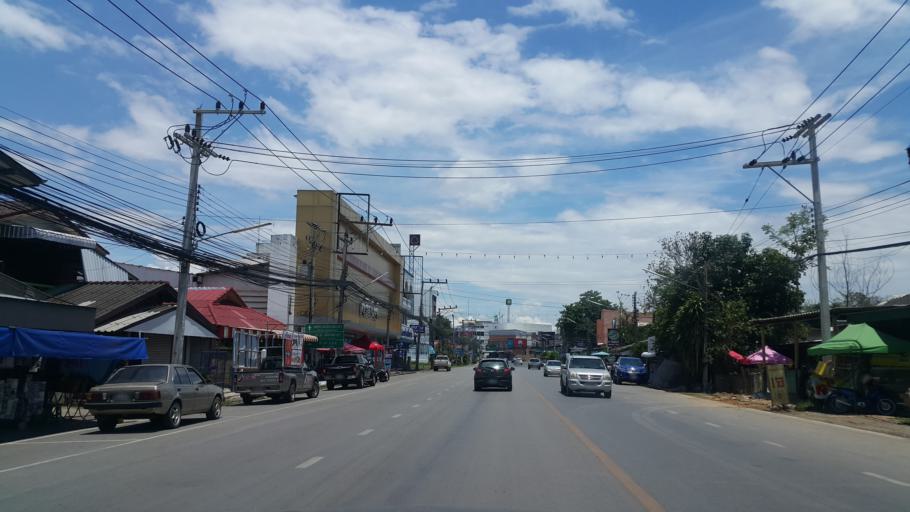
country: TH
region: Phayao
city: Phayao
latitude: 19.1717
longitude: 99.8954
